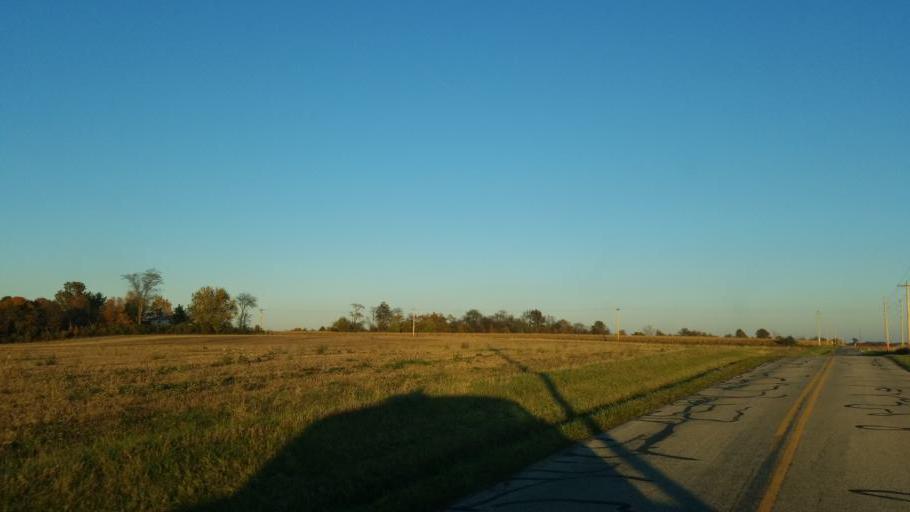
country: US
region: Ohio
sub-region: Huron County
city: Bellevue
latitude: 41.2118
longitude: -82.8819
